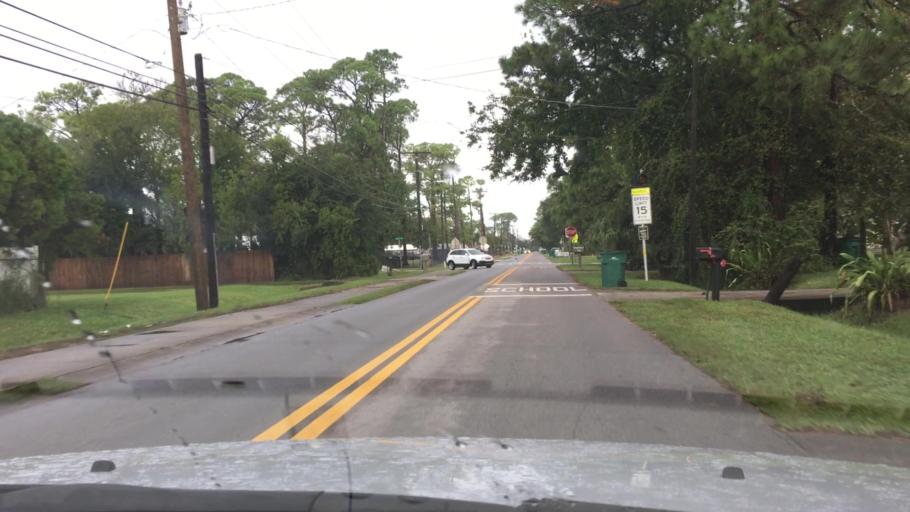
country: US
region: Florida
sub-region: Volusia County
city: Holly Hill
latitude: 29.2482
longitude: -81.0534
